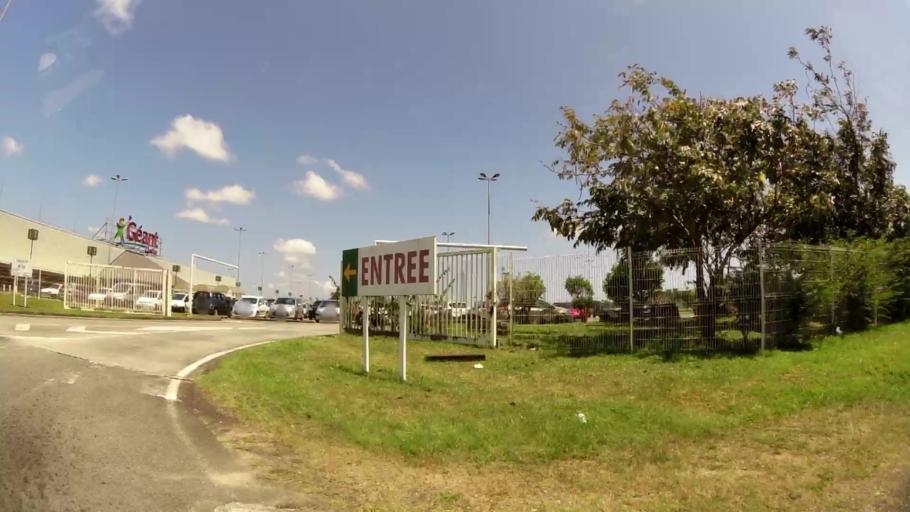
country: GF
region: Guyane
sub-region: Guyane
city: Cayenne
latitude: 4.9047
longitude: -52.3205
